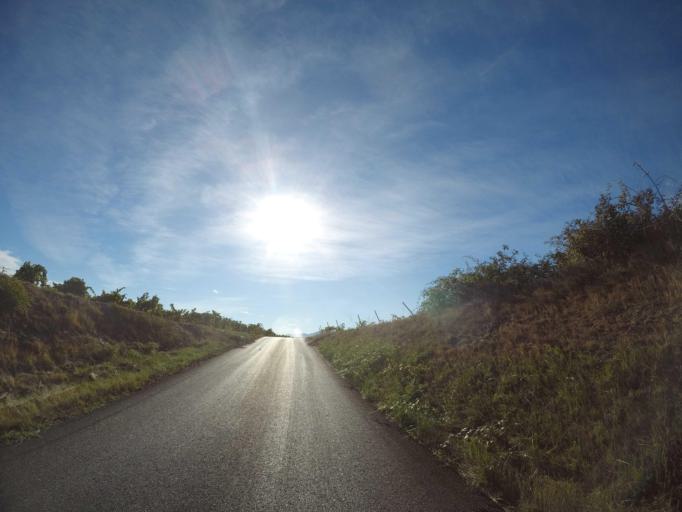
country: FR
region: Languedoc-Roussillon
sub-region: Departement des Pyrenees-Orientales
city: Llupia
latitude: 42.5888
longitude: 2.7651
